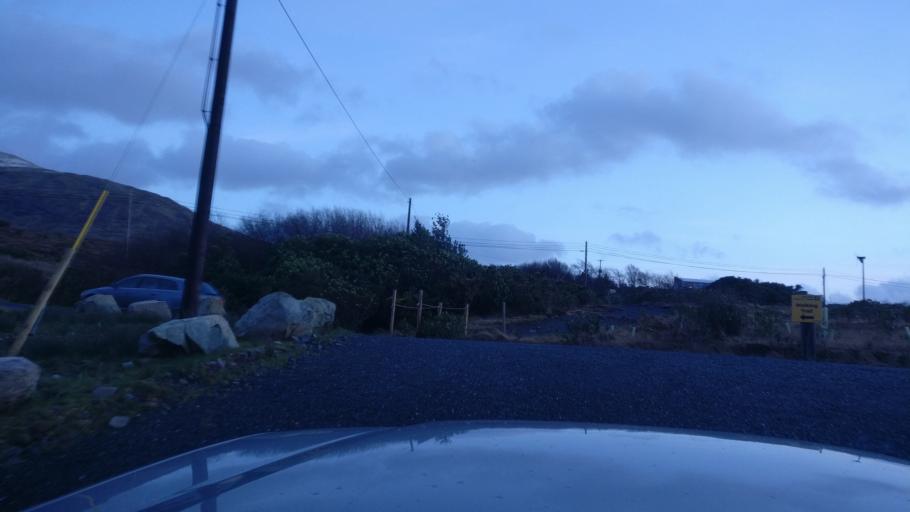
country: IE
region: Connaught
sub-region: County Galway
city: Clifden
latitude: 53.5945
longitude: -9.7697
